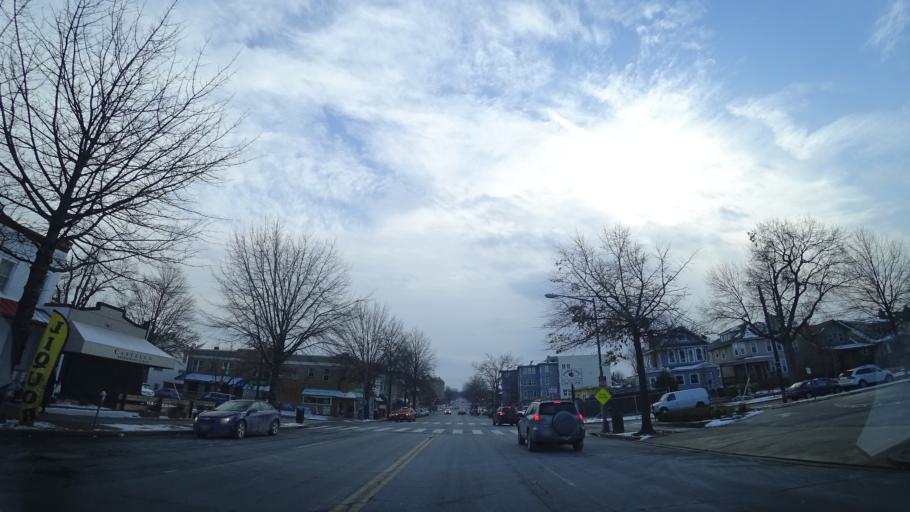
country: US
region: Maryland
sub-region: Montgomery County
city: Takoma Park
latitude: 38.9534
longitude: -77.0277
